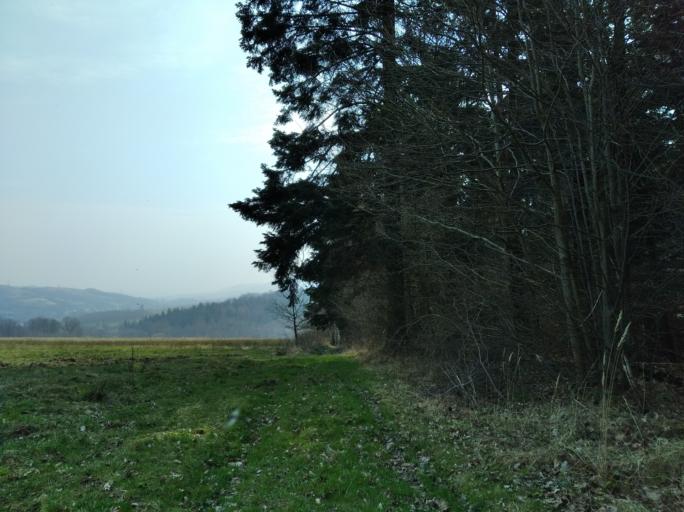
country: PL
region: Subcarpathian Voivodeship
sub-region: Powiat strzyzowski
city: Strzyzow
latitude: 49.8153
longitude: 21.8245
